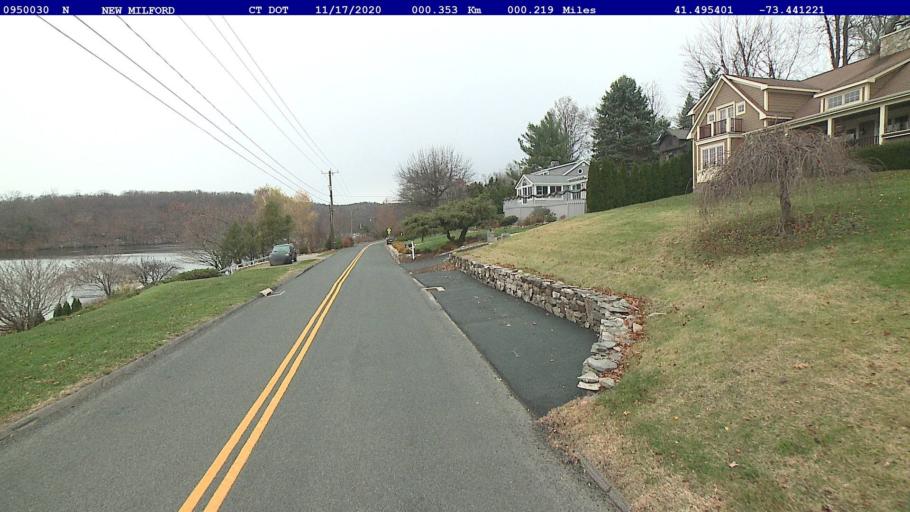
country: US
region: Connecticut
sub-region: Litchfield County
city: New Milford
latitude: 41.4954
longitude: -73.4412
